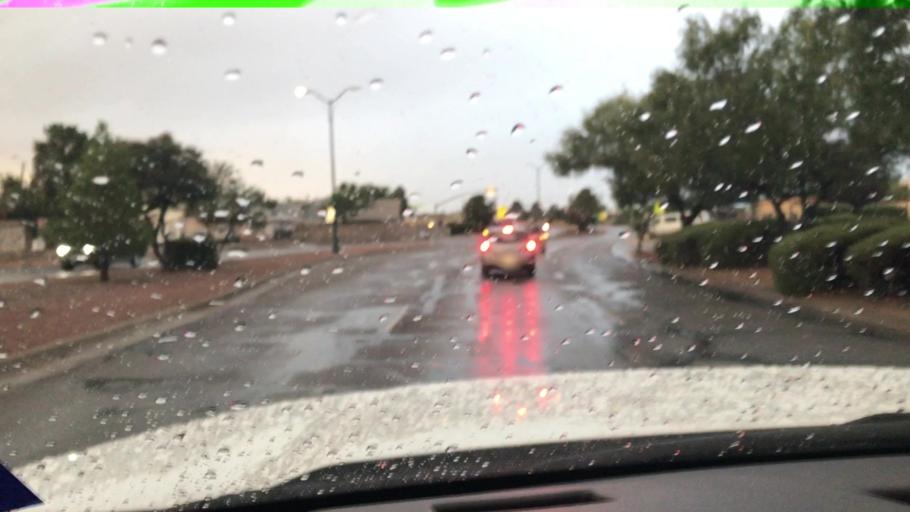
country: US
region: Texas
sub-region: El Paso County
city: Fort Bliss
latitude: 31.7981
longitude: -106.3227
